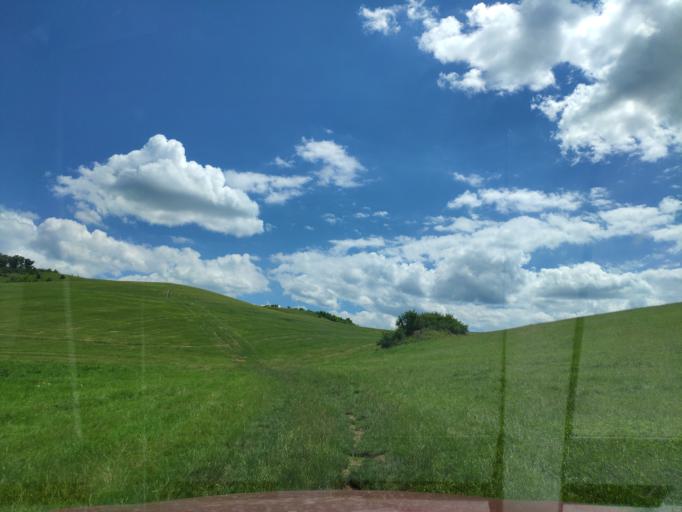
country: HU
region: Borsod-Abauj-Zemplen
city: Ozd
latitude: 48.2778
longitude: 20.2169
